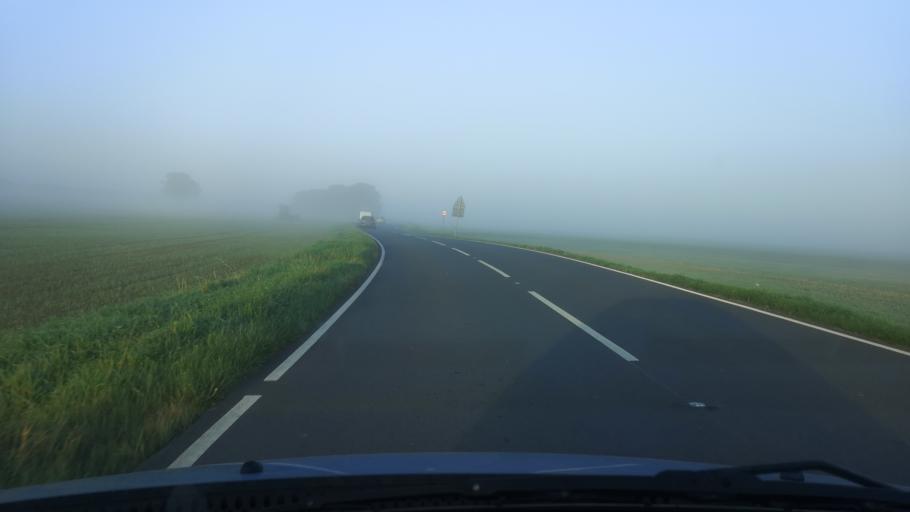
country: GB
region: England
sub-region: North Lincolnshire
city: Crowle
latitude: 53.6198
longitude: -0.8084
